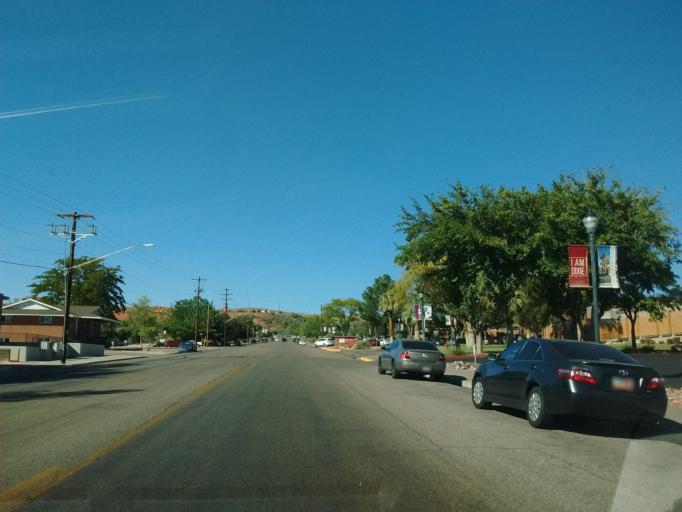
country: US
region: Utah
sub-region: Washington County
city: Saint George
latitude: 37.1035
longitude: -113.5684
